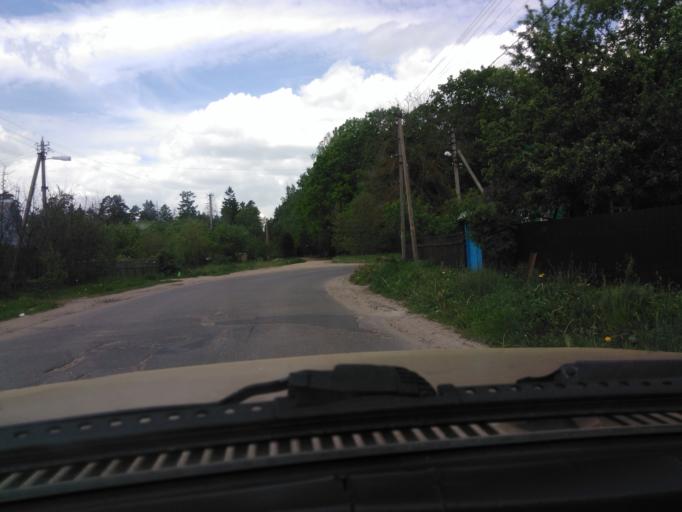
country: BY
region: Mogilev
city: Mahilyow
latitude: 53.9347
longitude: 30.3192
